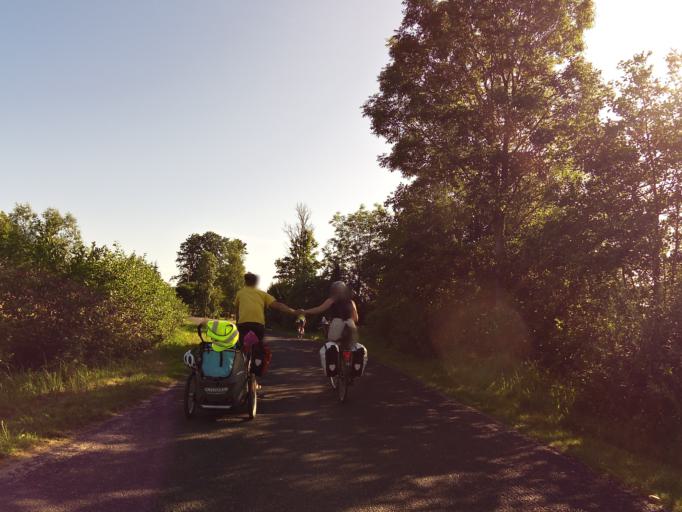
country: EE
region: Hiiumaa
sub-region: Kaerdla linn
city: Kardla
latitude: 58.7798
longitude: 22.4861
